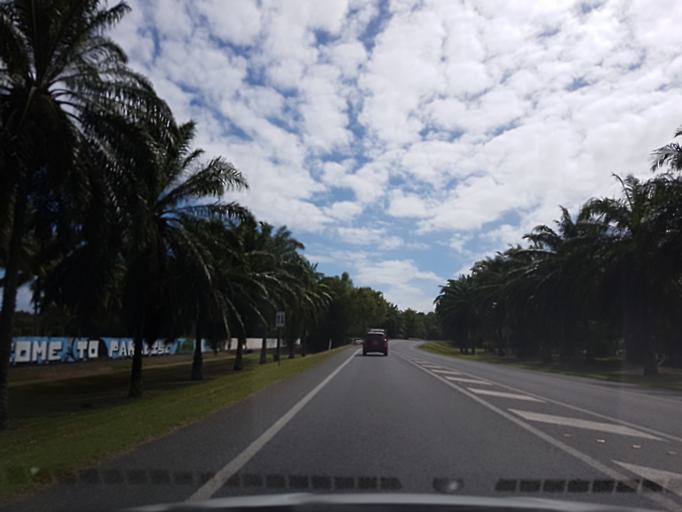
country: AU
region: Queensland
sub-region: Cairns
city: Port Douglas
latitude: -16.5089
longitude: 145.4630
